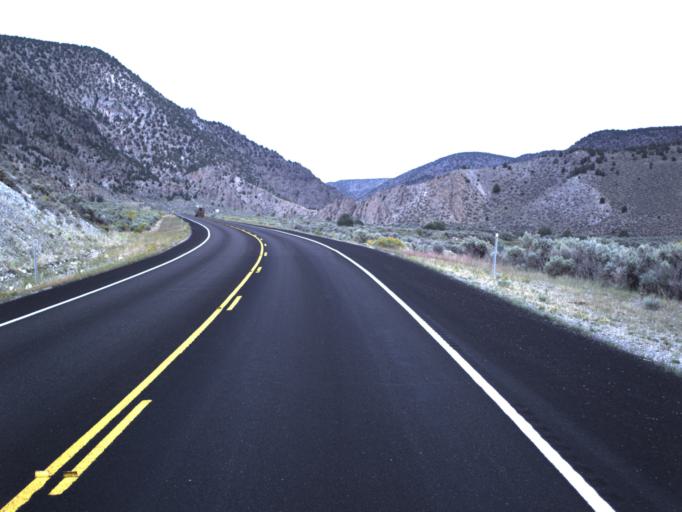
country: US
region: Utah
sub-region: Piute County
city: Junction
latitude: 38.0570
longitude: -112.3491
